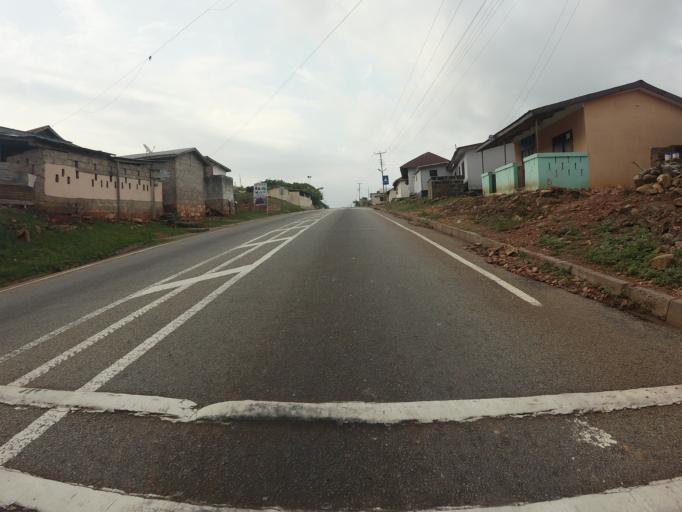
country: GH
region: Volta
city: Ho
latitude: 6.6581
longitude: 0.4713
